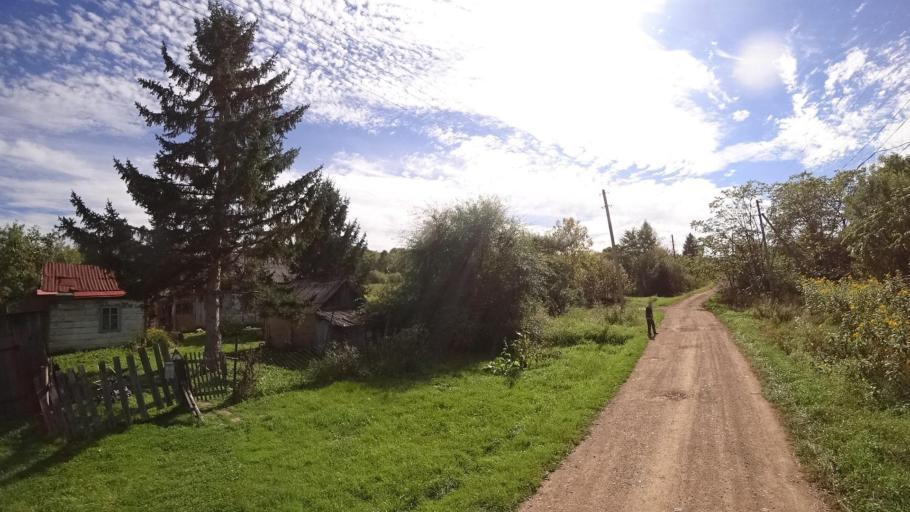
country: RU
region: Primorskiy
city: Yakovlevka
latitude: 44.3893
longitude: 133.6040
